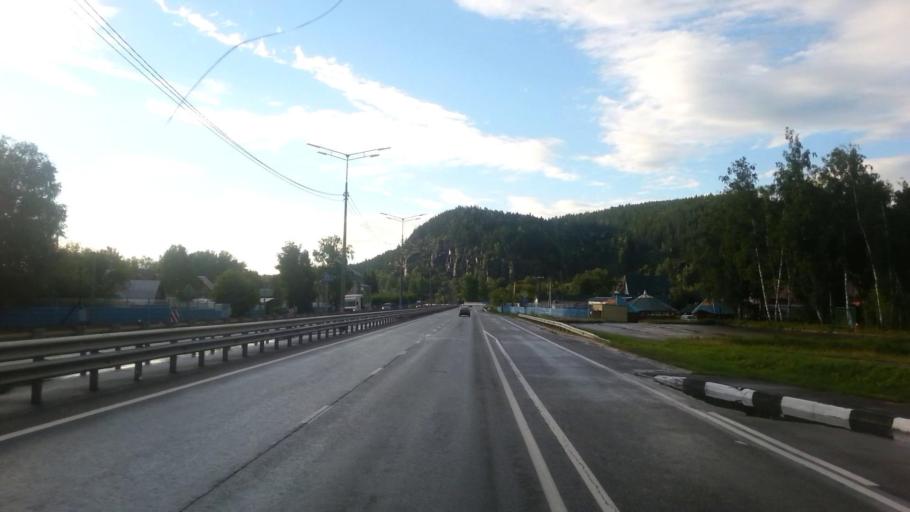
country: RU
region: Altay
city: Souzga
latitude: 51.9147
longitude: 85.8626
